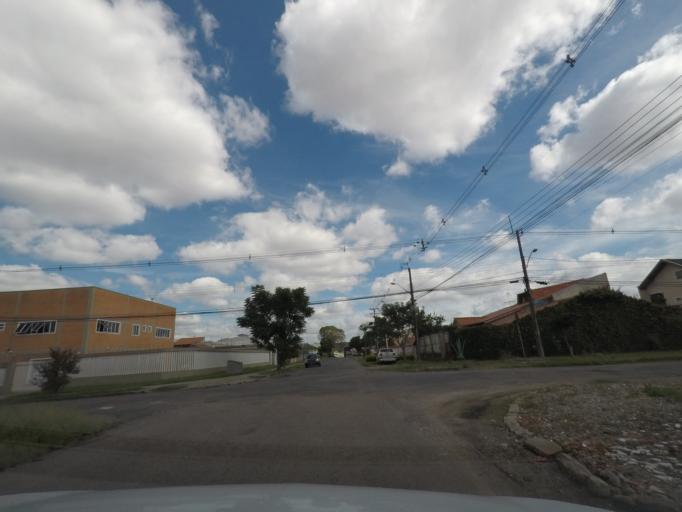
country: BR
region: Parana
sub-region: Sao Jose Dos Pinhais
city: Sao Jose dos Pinhais
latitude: -25.5042
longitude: -49.2232
